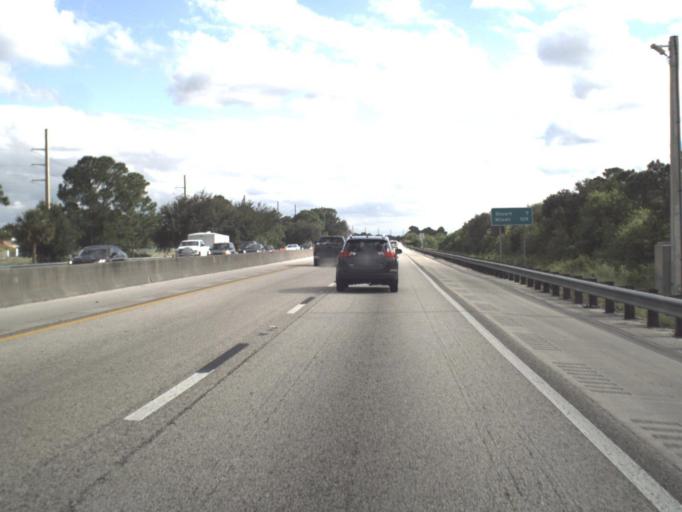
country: US
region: Florida
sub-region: Saint Lucie County
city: Port Saint Lucie
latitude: 27.2671
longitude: -80.3550
